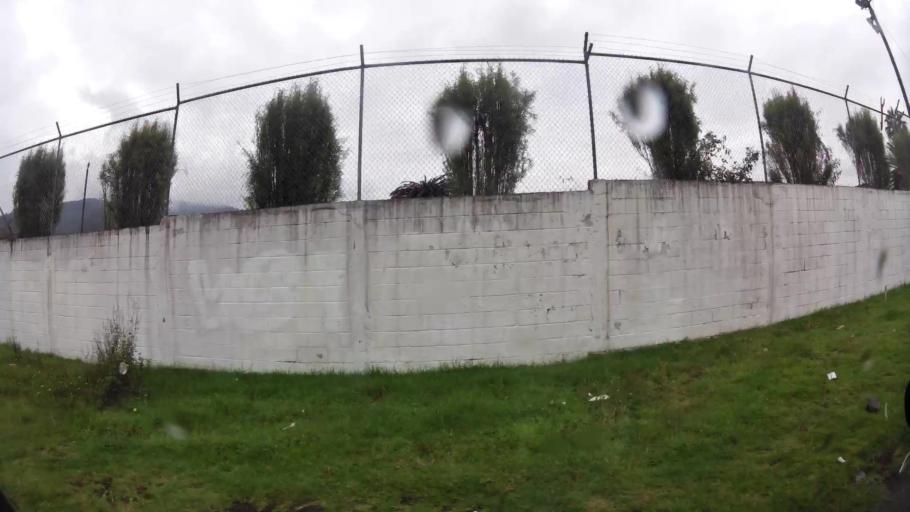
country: EC
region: Pichincha
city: Sangolqui
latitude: -0.2860
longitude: -78.4505
